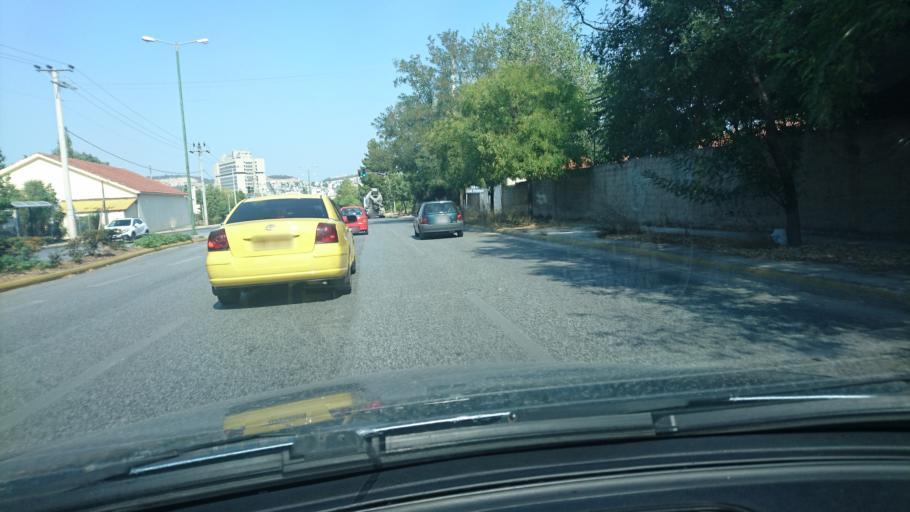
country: GR
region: Attica
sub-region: Nomarchia Athinas
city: Papagou
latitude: 37.9855
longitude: 23.7819
